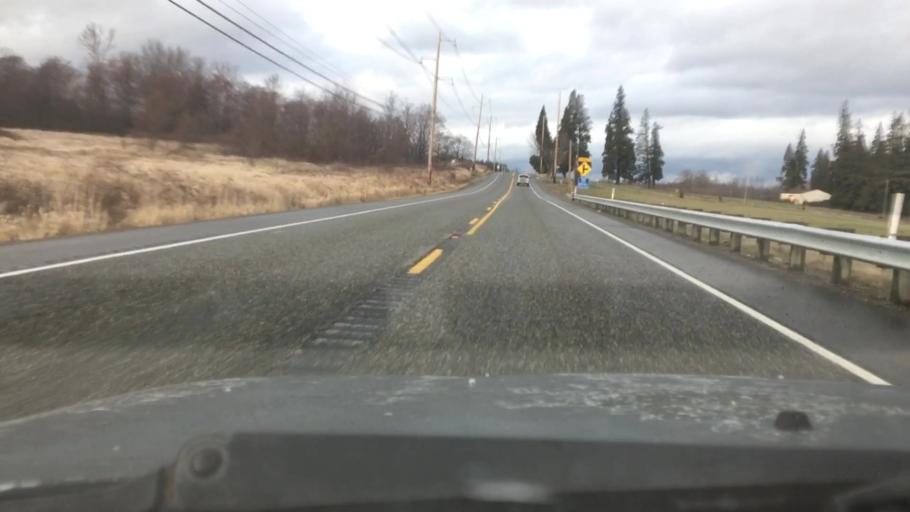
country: US
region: Washington
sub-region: Whatcom County
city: Ferndale
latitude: 48.8394
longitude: -122.6825
